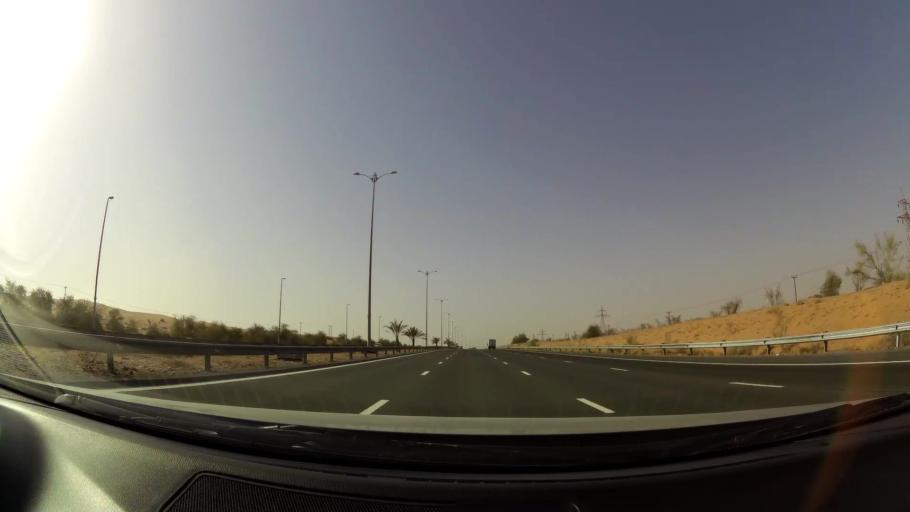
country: OM
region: Al Buraimi
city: Al Buraymi
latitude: 24.6201
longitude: 55.7257
